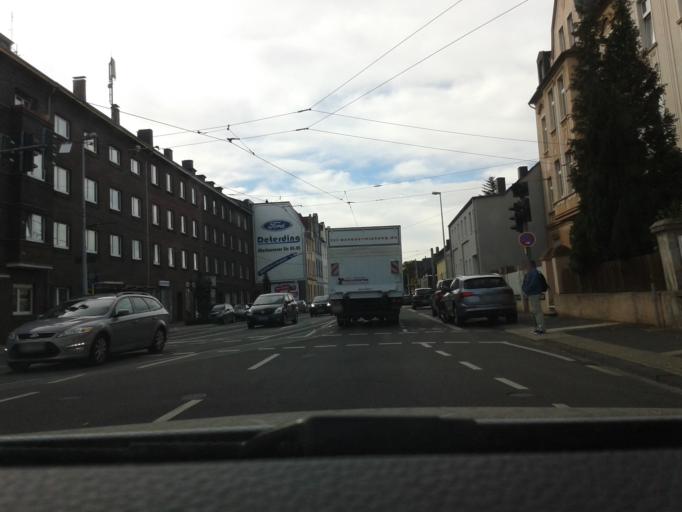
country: DE
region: North Rhine-Westphalia
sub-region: Regierungsbezirk Dusseldorf
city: Muelheim (Ruhr)
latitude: 51.4490
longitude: 6.8503
